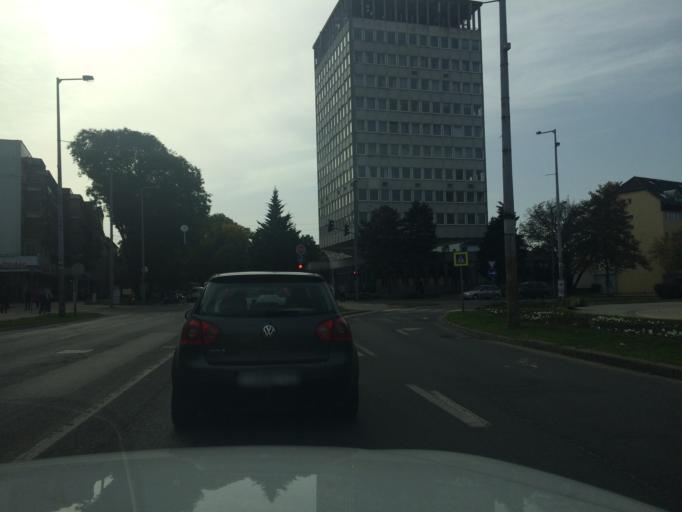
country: HU
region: Szabolcs-Szatmar-Bereg
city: Nyiregyhaza
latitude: 47.9535
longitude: 21.7156
